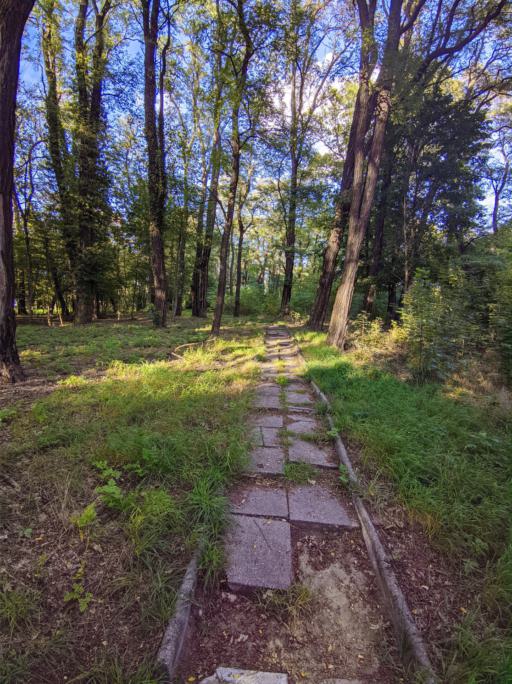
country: PL
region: Lubusz
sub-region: Powiat zarski
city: Jasien
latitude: 51.7530
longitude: 15.0167
